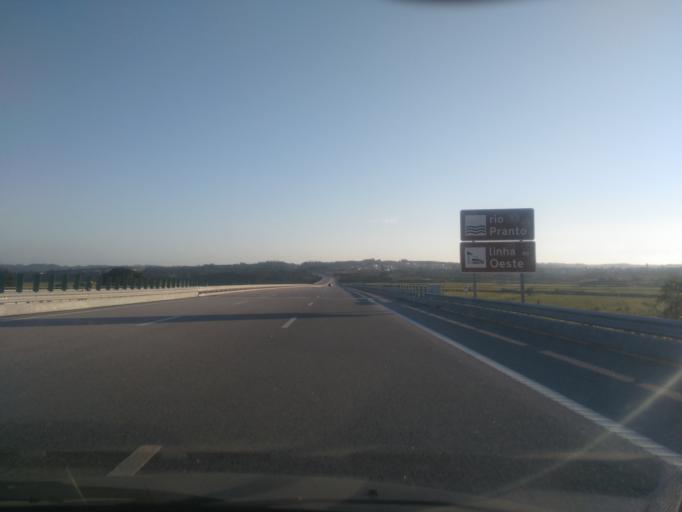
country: PT
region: Coimbra
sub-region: Figueira da Foz
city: Lavos
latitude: 40.1027
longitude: -8.7474
